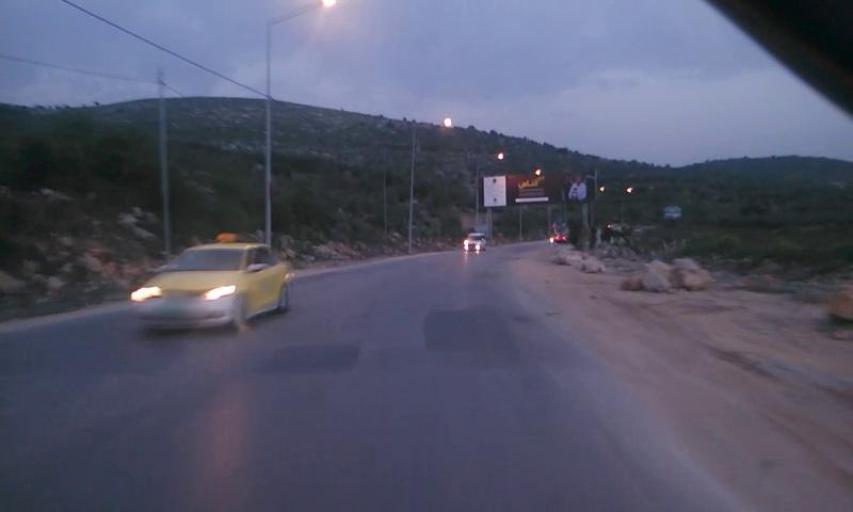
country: PS
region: West Bank
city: `Anabta
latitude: 32.3021
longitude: 35.1310
